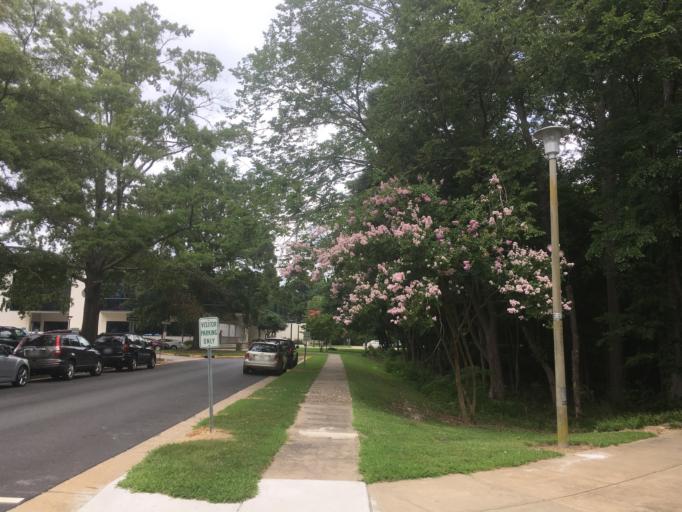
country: US
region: Virginia
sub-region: City of Chesapeake
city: Chesapeake
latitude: 36.7160
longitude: -76.2481
